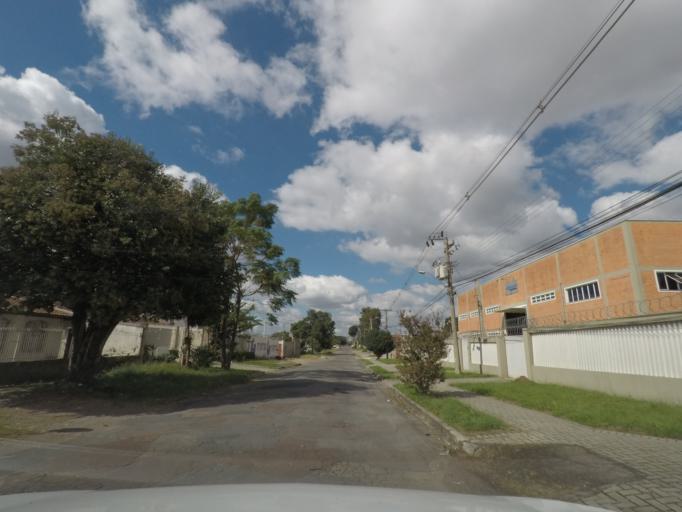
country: BR
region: Parana
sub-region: Sao Jose Dos Pinhais
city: Sao Jose dos Pinhais
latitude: -25.5043
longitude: -49.2234
